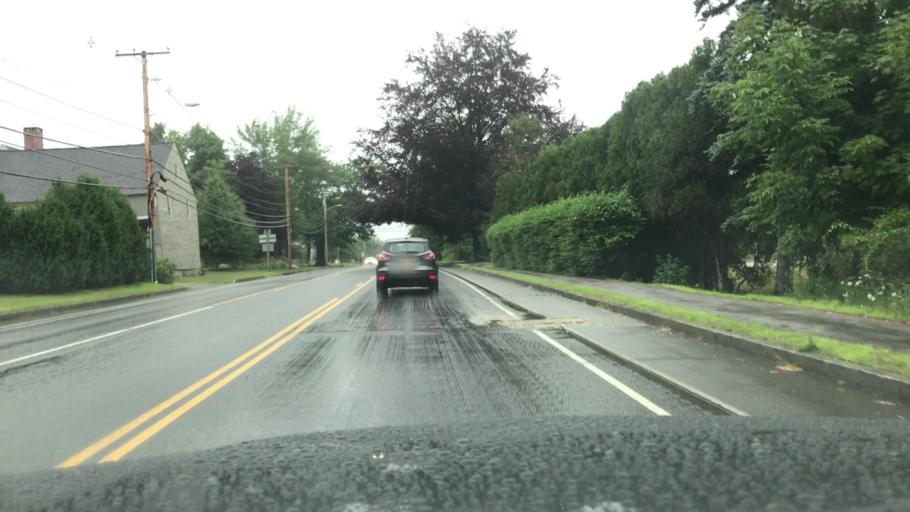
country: US
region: Maine
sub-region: York County
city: Kennebunk
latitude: 43.3893
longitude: -70.5363
